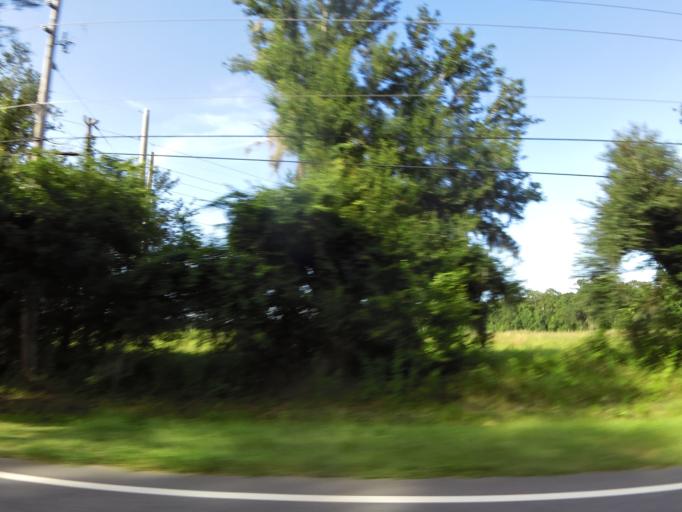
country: US
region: Florida
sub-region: Clay County
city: Green Cove Springs
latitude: 29.9860
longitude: -81.5268
